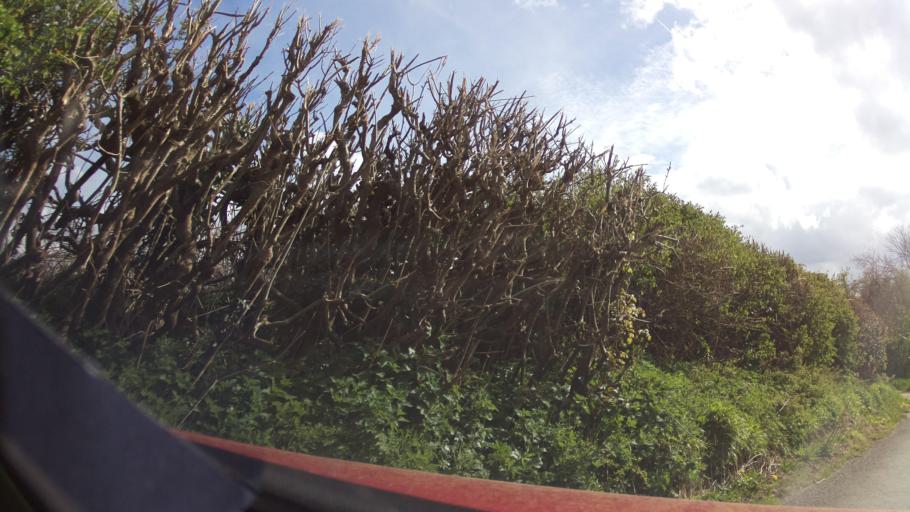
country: GB
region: England
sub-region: Hampshire
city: Romsey
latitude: 51.0892
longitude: -1.5119
